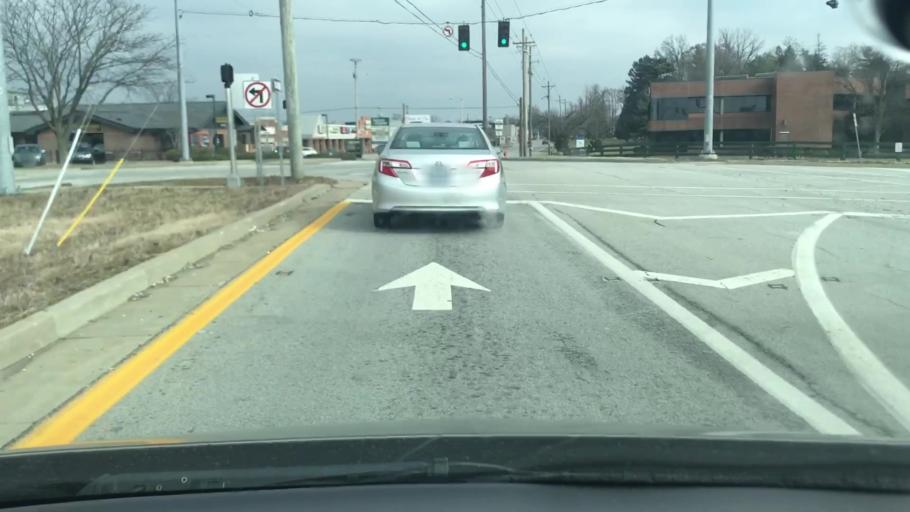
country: US
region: Kentucky
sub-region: Jefferson County
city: Windy Hills
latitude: 38.2805
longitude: -85.6339
